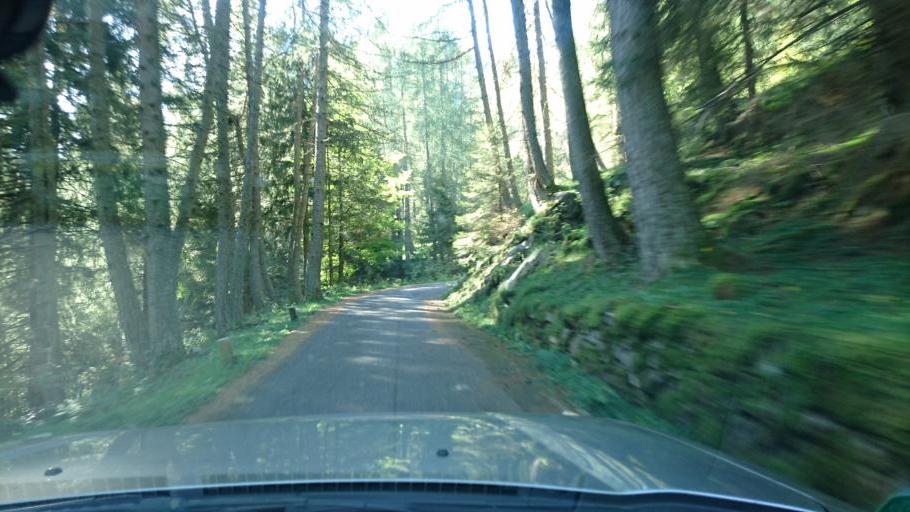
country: IT
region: Lombardy
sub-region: Provincia di Brescia
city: Lozio
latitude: 46.0481
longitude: 10.2233
